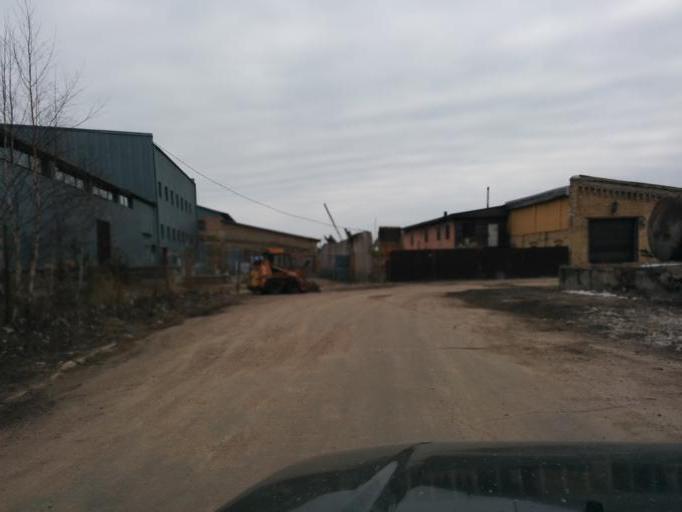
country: LV
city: Tireli
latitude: 56.9453
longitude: 23.6343
